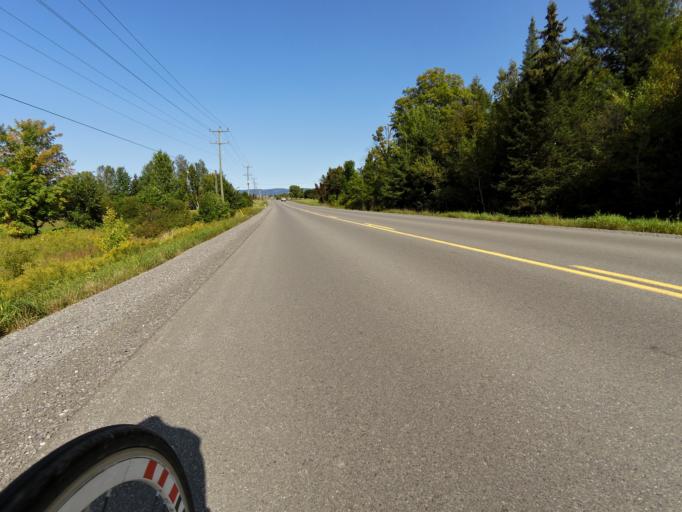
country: CA
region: Ontario
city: Arnprior
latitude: 45.4395
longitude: -76.1100
